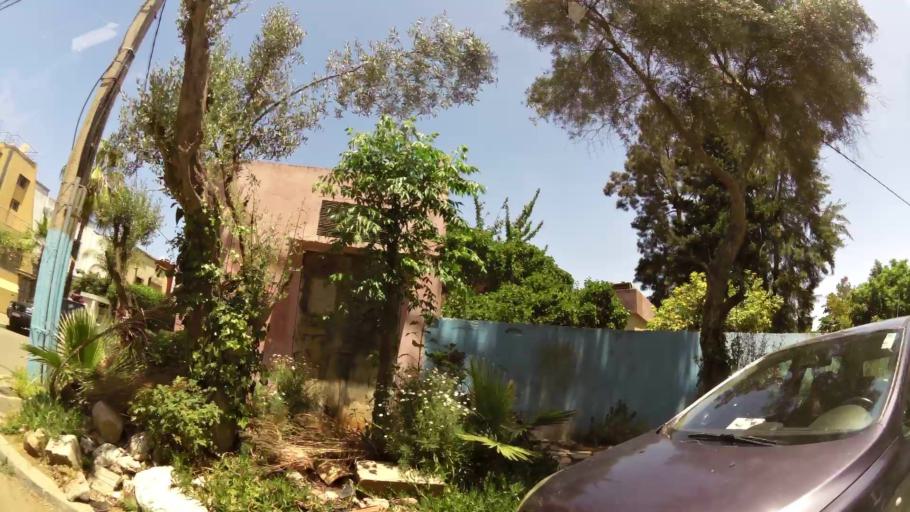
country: MA
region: Gharb-Chrarda-Beni Hssen
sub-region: Kenitra Province
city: Kenitra
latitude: 34.2630
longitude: -6.6217
